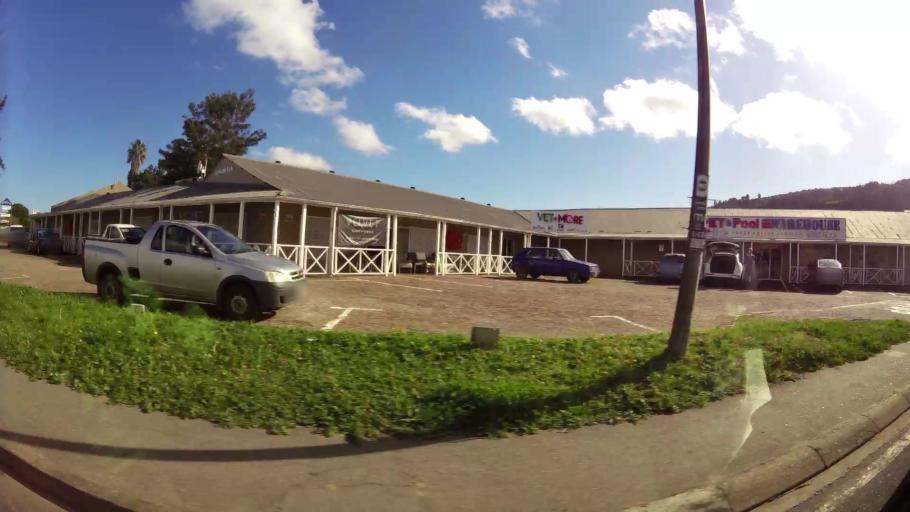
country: ZA
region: Western Cape
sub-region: Eden District Municipality
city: Knysna
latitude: -34.0399
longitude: 23.0530
